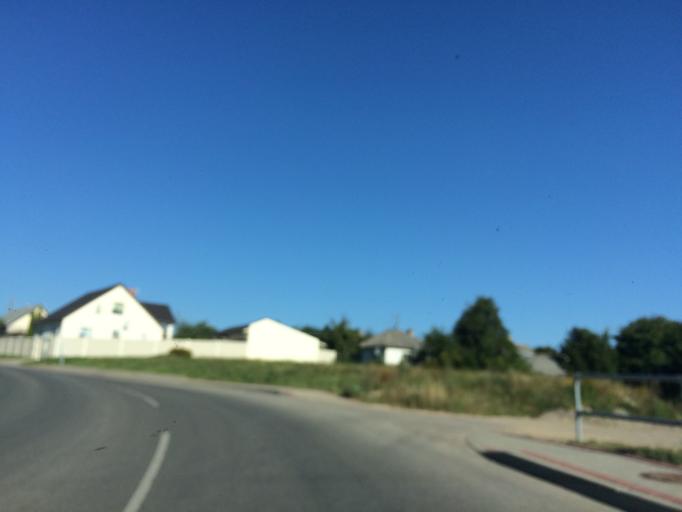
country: LV
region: Rezekne
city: Rezekne
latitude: 56.5114
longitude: 27.3492
